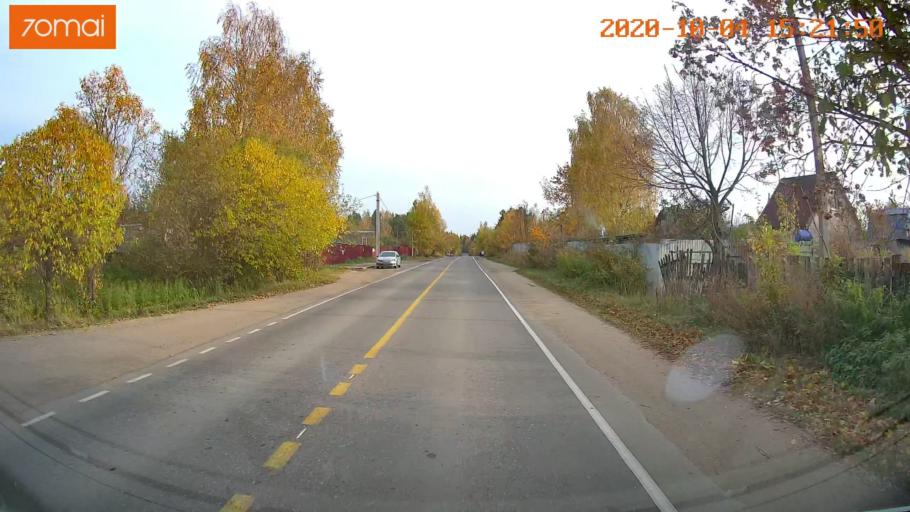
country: RU
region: Ivanovo
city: Bogorodskoye
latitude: 57.0841
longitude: 40.9272
